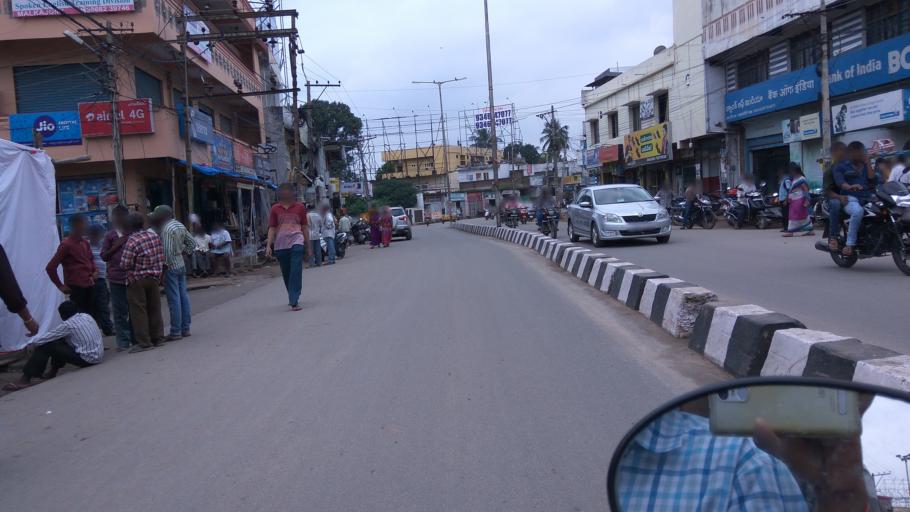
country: IN
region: Telangana
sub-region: Hyderabad
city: Malkajgiri
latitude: 17.4493
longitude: 78.5361
